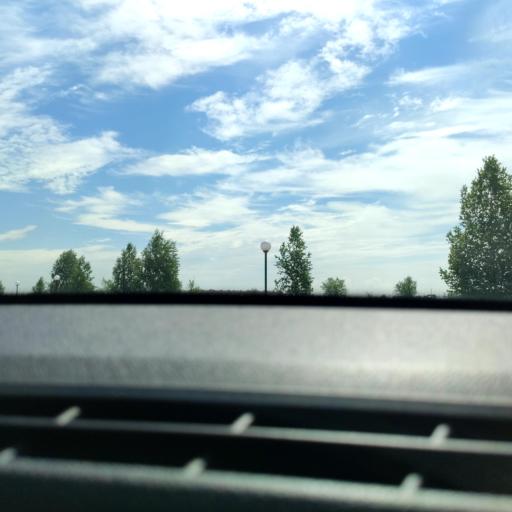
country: RU
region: Samara
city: Podstepki
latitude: 53.5275
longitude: 49.1807
